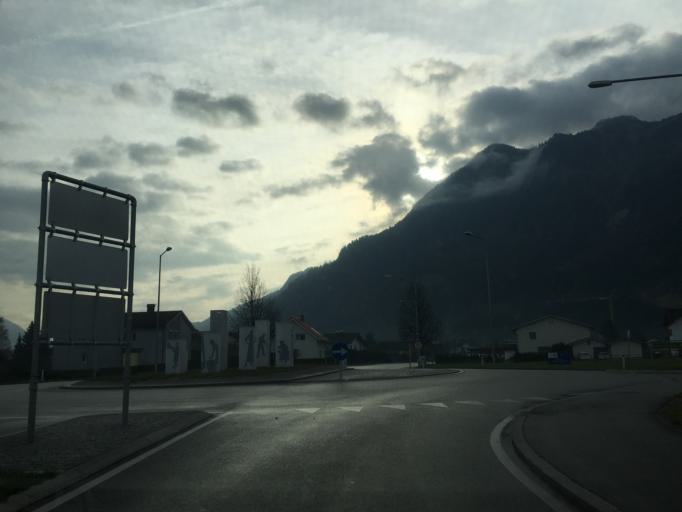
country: AT
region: Vorarlberg
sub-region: Politischer Bezirk Bludenz
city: Nenzing
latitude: 47.1868
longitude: 9.7100
